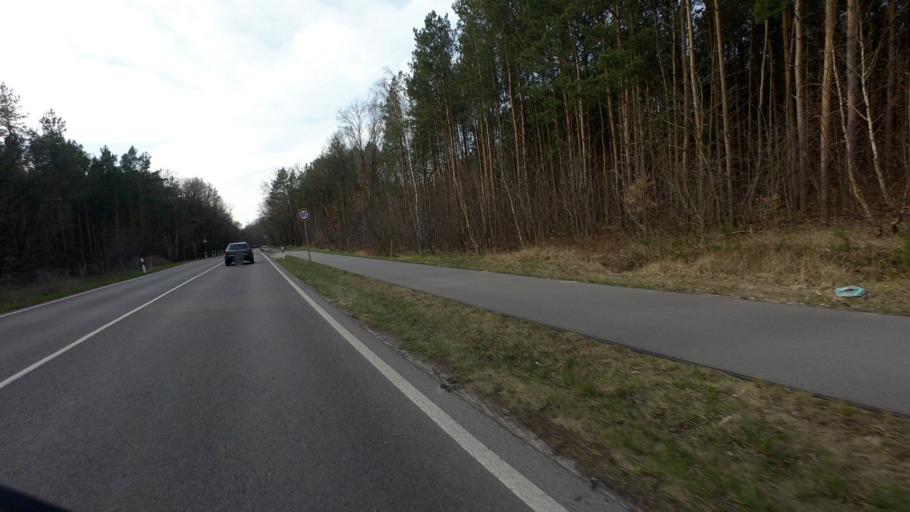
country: DE
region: Berlin
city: Wannsee
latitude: 52.3764
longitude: 13.1608
